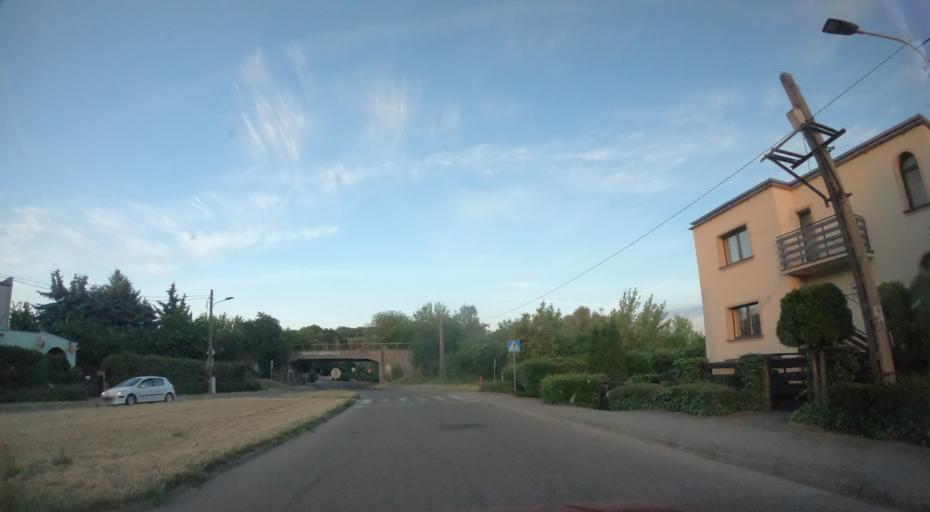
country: PL
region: Lubusz
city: Gorzow Wielkopolski
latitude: 52.7349
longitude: 15.2814
